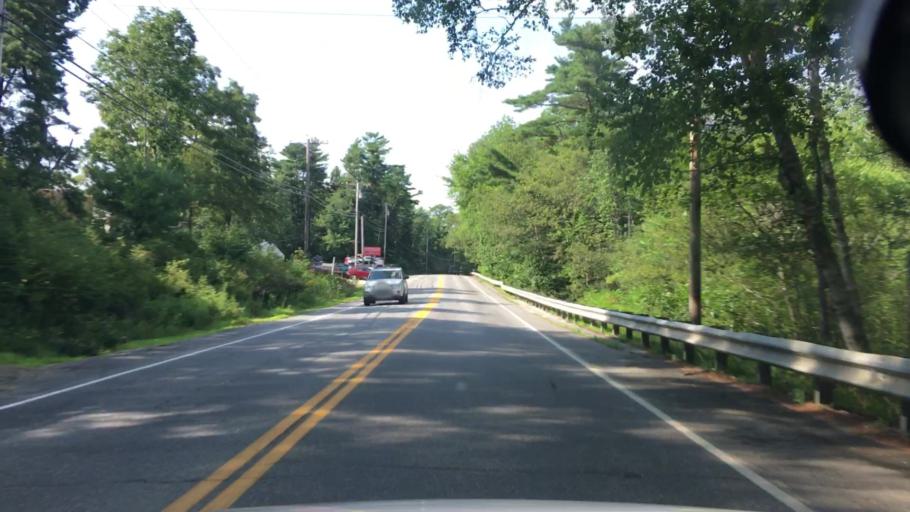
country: US
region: Maine
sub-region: Cumberland County
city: Harpswell Center
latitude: 43.8399
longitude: -69.9120
